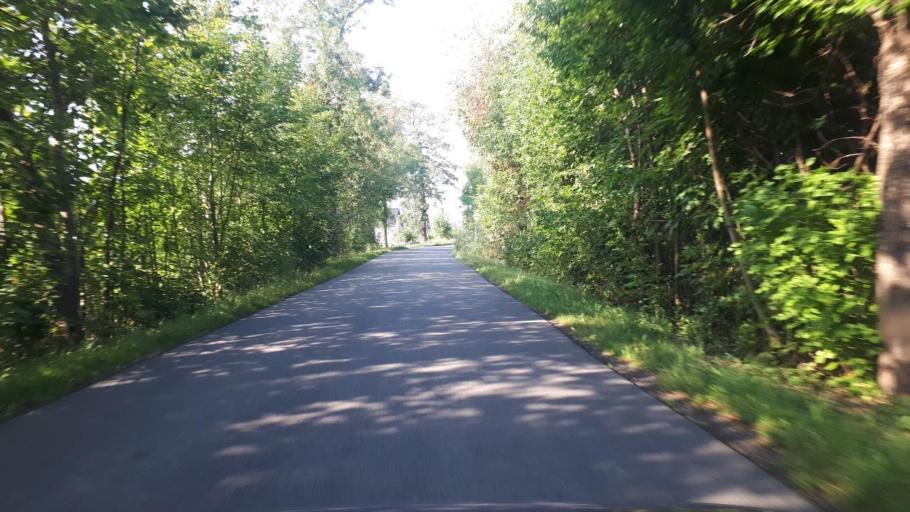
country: PL
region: Silesian Voivodeship
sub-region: Powiat cieszynski
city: Chybie
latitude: 49.8636
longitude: 18.8598
